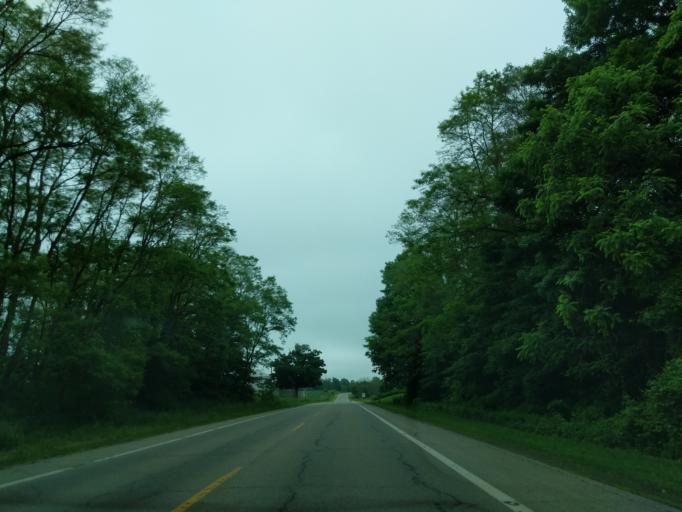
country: US
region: Michigan
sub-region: Hillsdale County
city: Litchfield
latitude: 42.0290
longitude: -84.7203
